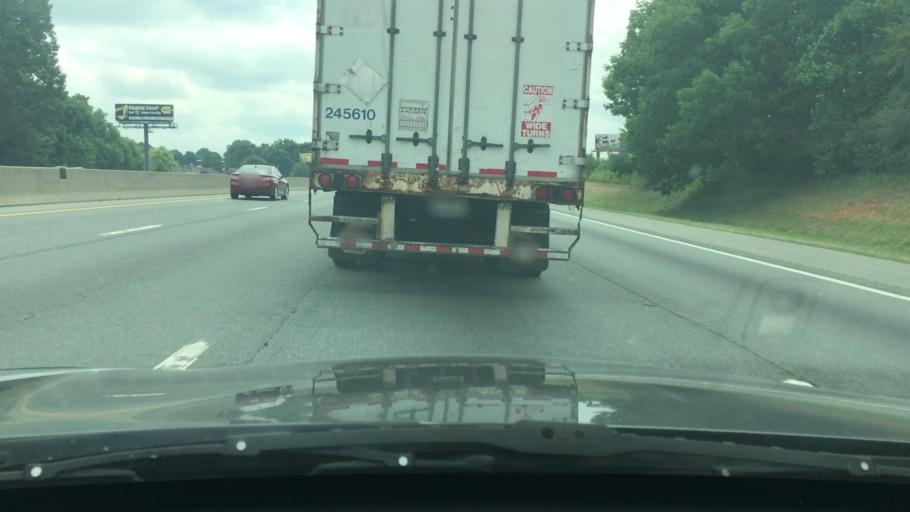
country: US
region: North Carolina
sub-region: Alamance County
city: Haw River
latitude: 36.0684
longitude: -79.3362
